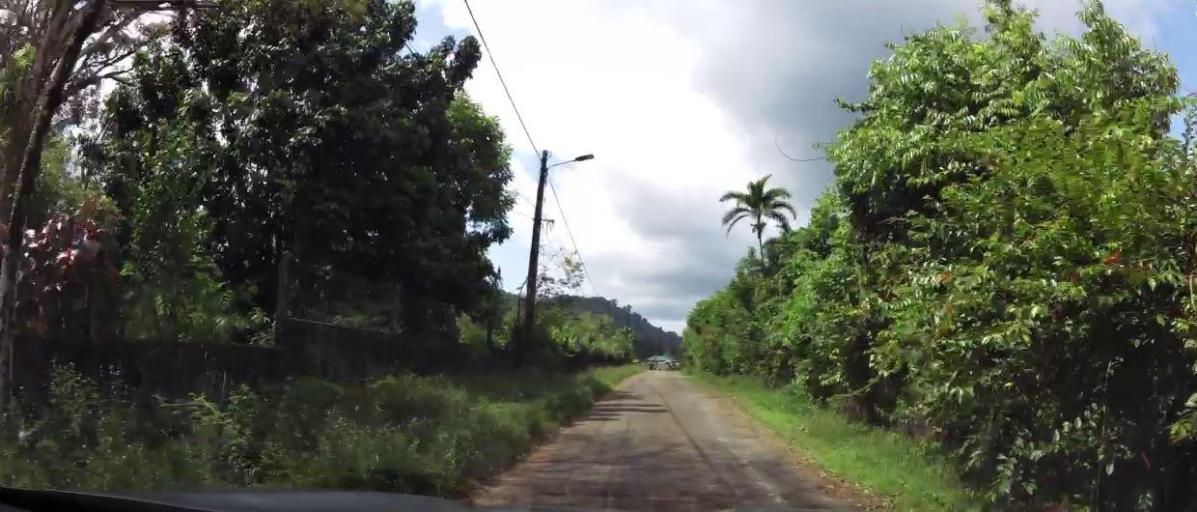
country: GF
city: Macouria
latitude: 4.8809
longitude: -52.3598
